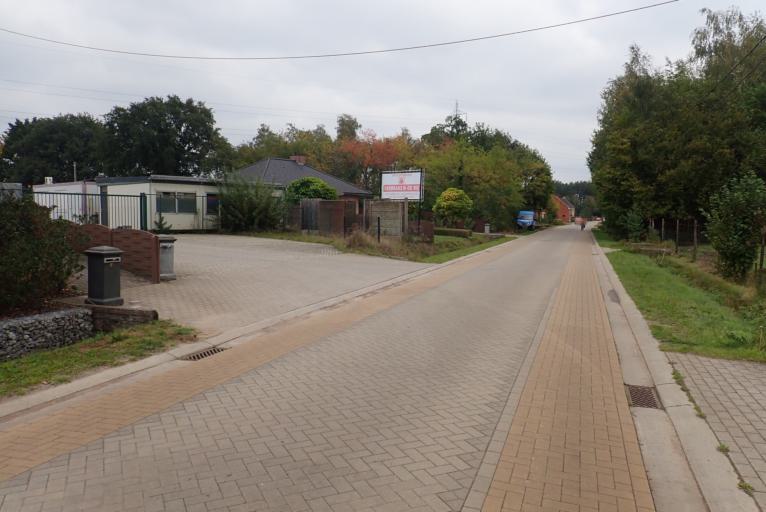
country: BE
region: Flanders
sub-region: Provincie Antwerpen
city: Lille
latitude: 51.2335
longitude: 4.8166
